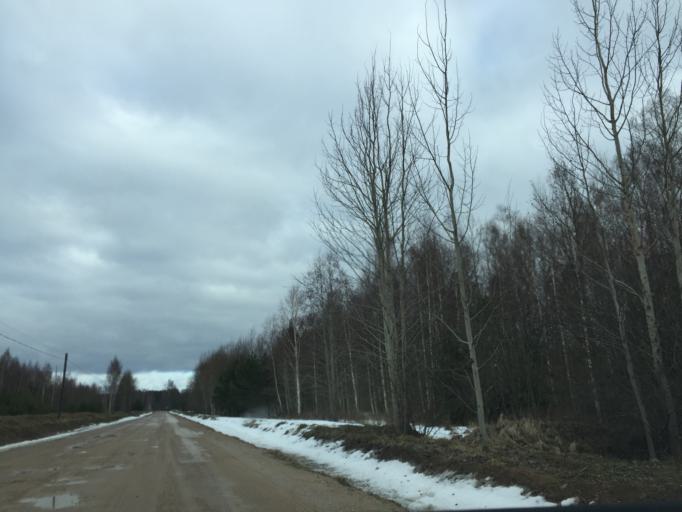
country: LV
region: Salacgrivas
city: Ainazi
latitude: 57.8547
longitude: 24.4940
